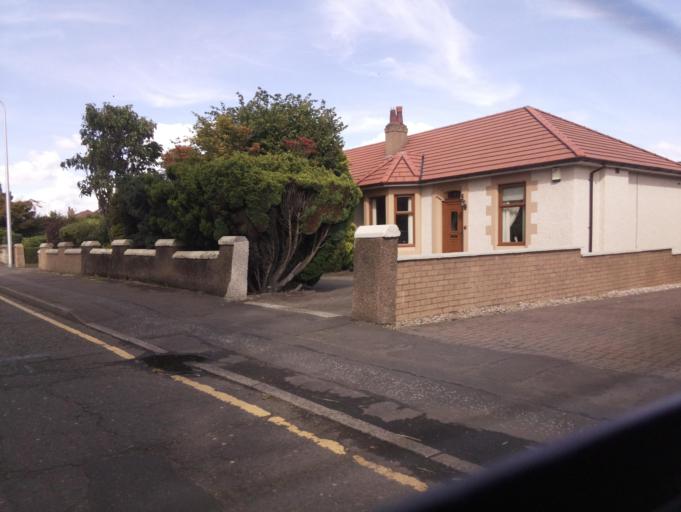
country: GB
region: Scotland
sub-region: Falkirk
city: Larbert
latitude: 56.0215
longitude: -3.8369
